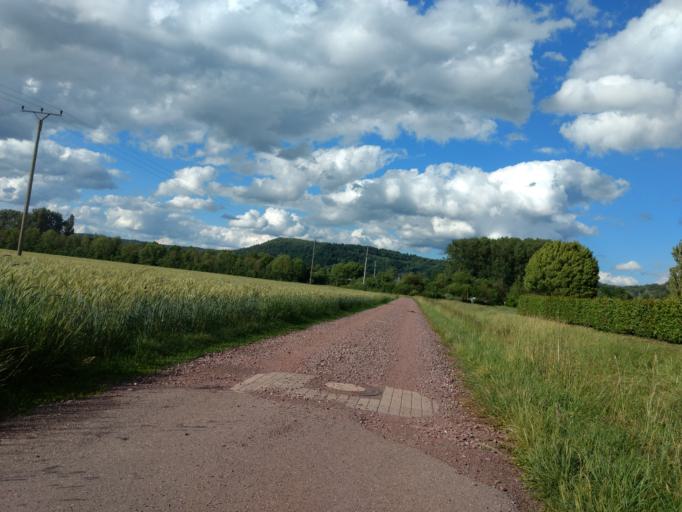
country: DE
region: Saarland
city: Merzig
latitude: 49.4453
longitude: 6.6192
